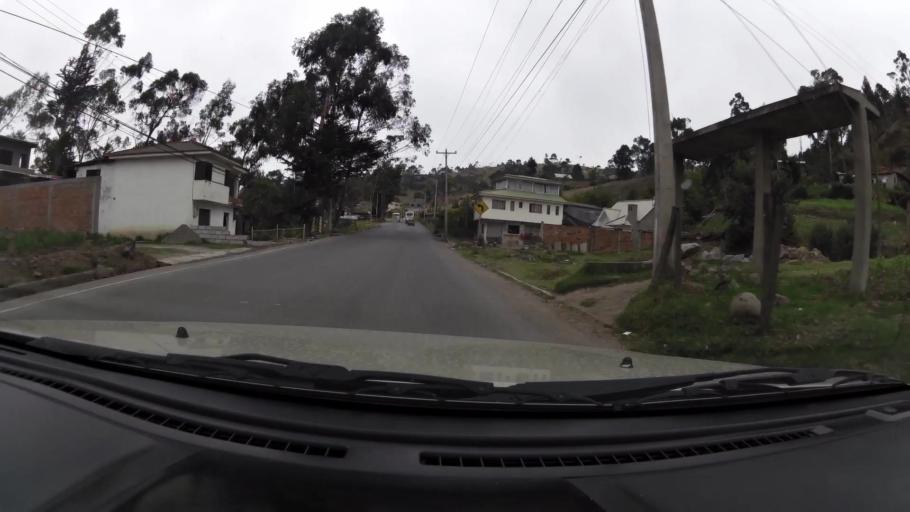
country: EC
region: Canar
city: Canar
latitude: -2.5020
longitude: -78.9305
